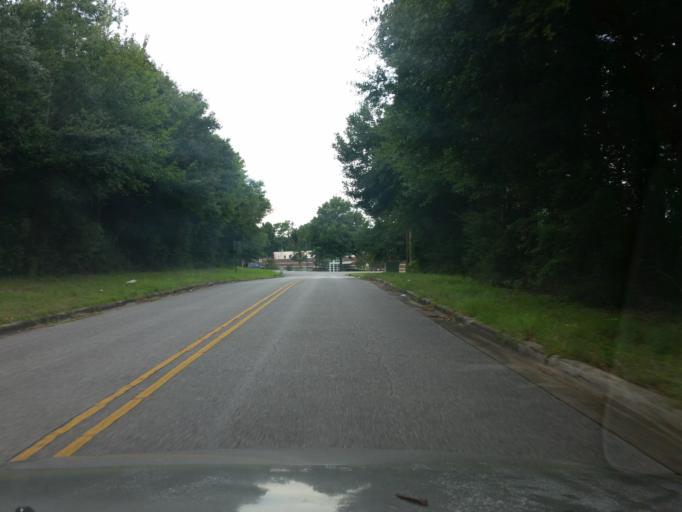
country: US
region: Florida
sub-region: Escambia County
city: Brent
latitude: 30.4752
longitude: -87.2688
